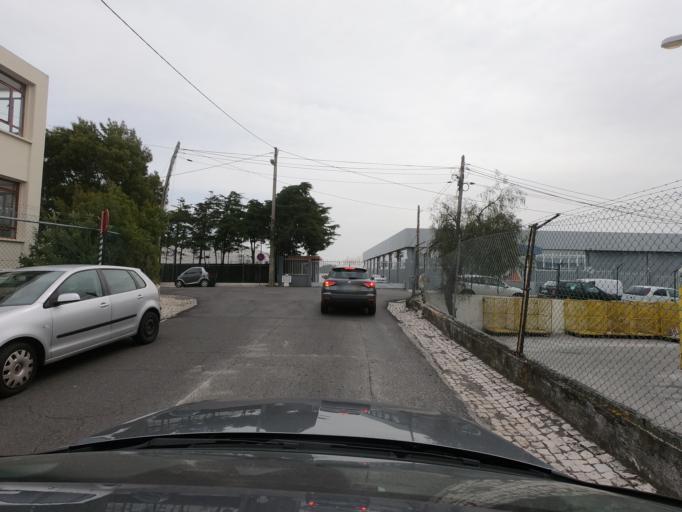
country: PT
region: Lisbon
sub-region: Oeiras
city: Barcarena
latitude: 38.7388
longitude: -9.2677
